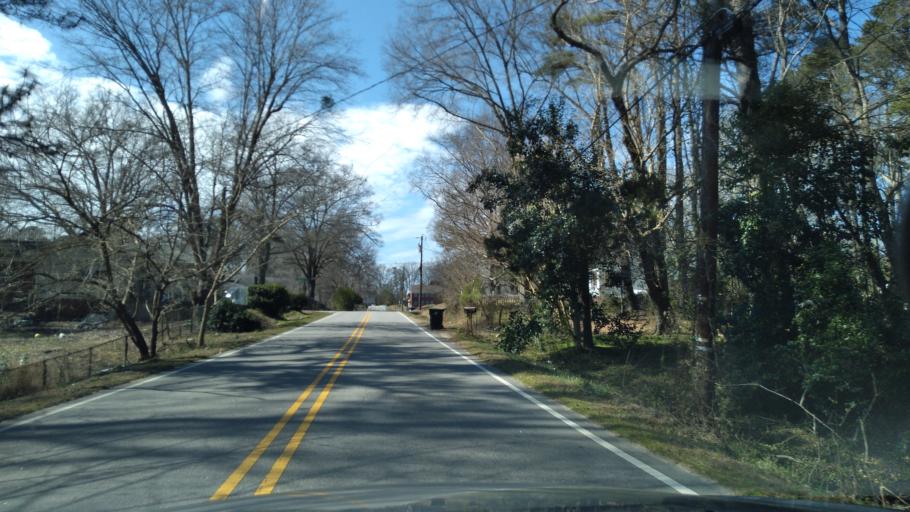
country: US
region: North Carolina
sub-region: Wake County
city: Garner
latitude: 35.7097
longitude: -78.6528
